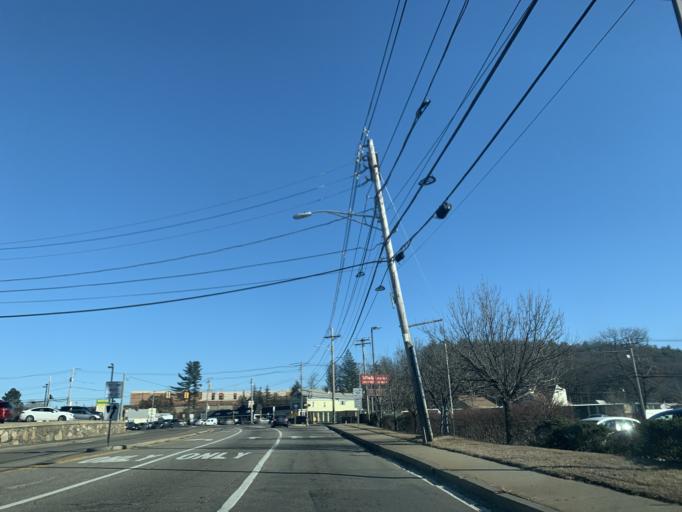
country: US
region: Massachusetts
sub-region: Middlesex County
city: Marlborough
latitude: 42.3477
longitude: -71.5095
